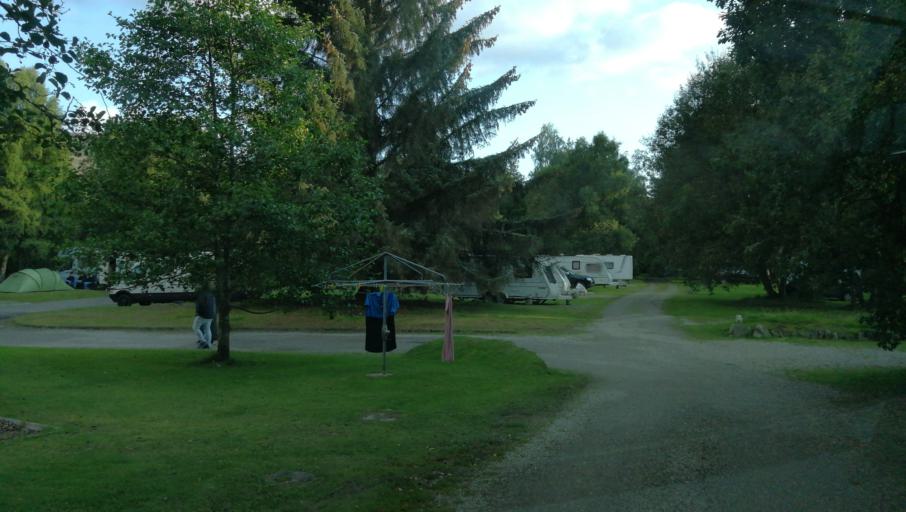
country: GB
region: Scotland
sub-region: Highland
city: Beauly
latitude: 57.3442
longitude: -4.7588
